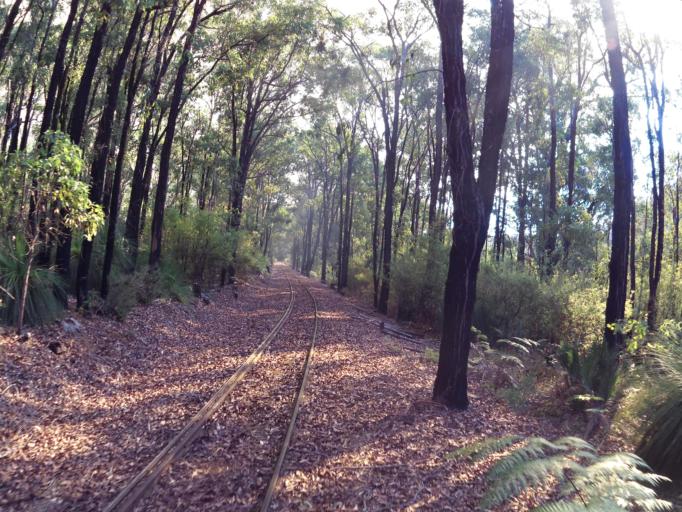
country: AU
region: Western Australia
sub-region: Waroona
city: Waroona
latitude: -32.7368
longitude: 116.1355
